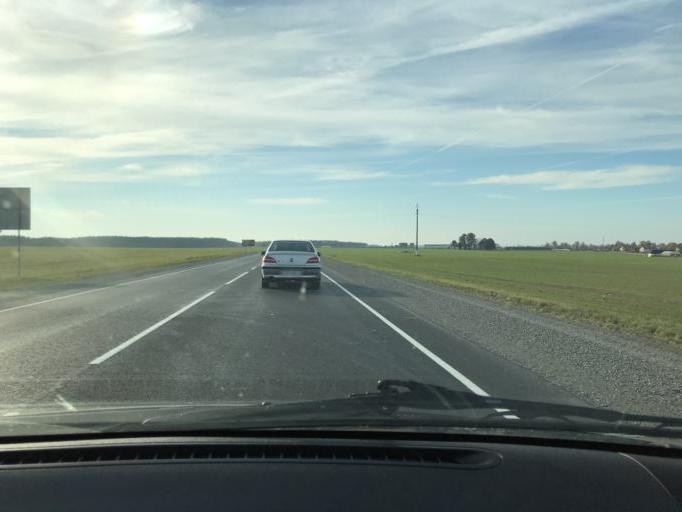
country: BY
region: Brest
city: Horad Pinsk
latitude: 52.1675
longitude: 26.0145
